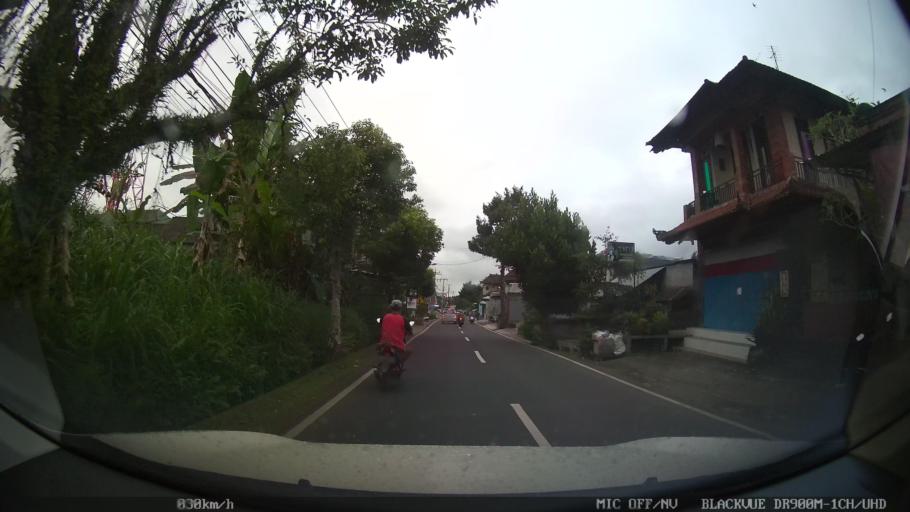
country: ID
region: Bali
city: Badung
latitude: -8.4207
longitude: 115.2452
